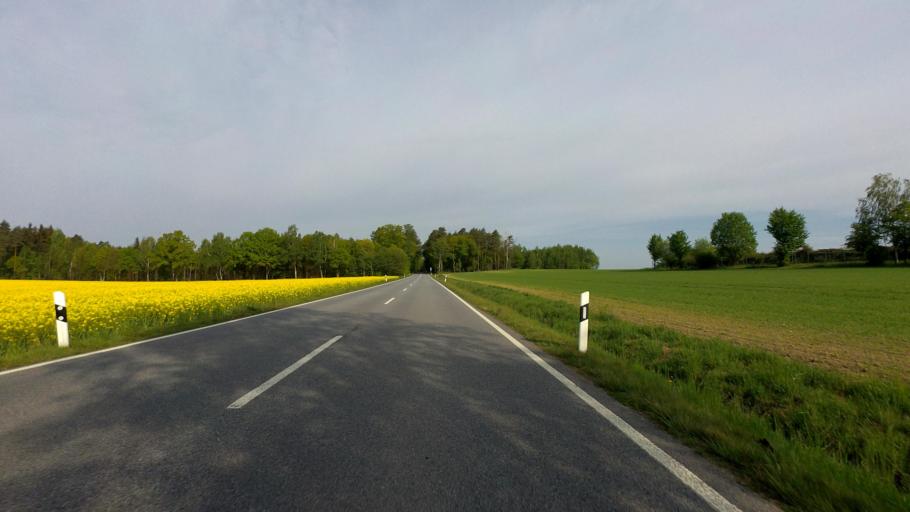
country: DE
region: Saxony
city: Stolpen
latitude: 51.0691
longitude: 14.0466
